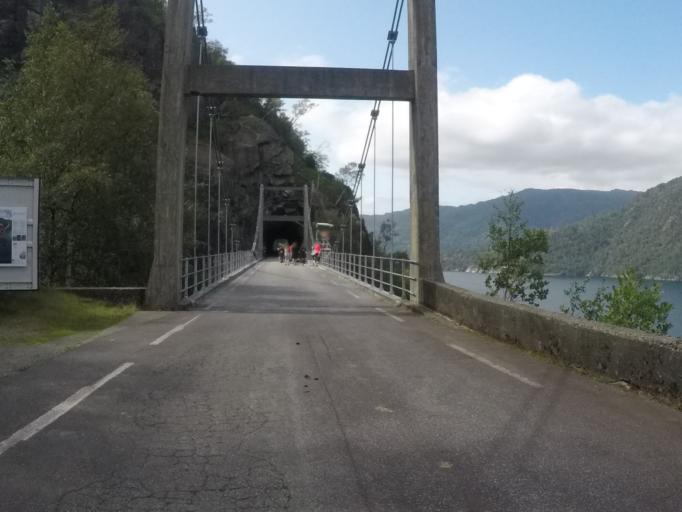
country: NO
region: Rogaland
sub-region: Sauda
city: Sauda
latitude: 59.7856
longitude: 6.1590
